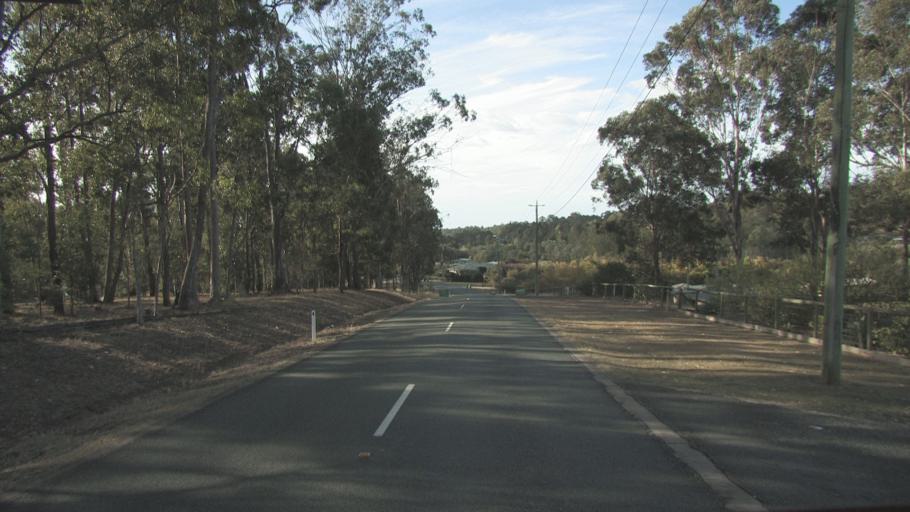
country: AU
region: Queensland
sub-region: Logan
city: Cedar Vale
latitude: -27.8829
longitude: 153.0100
